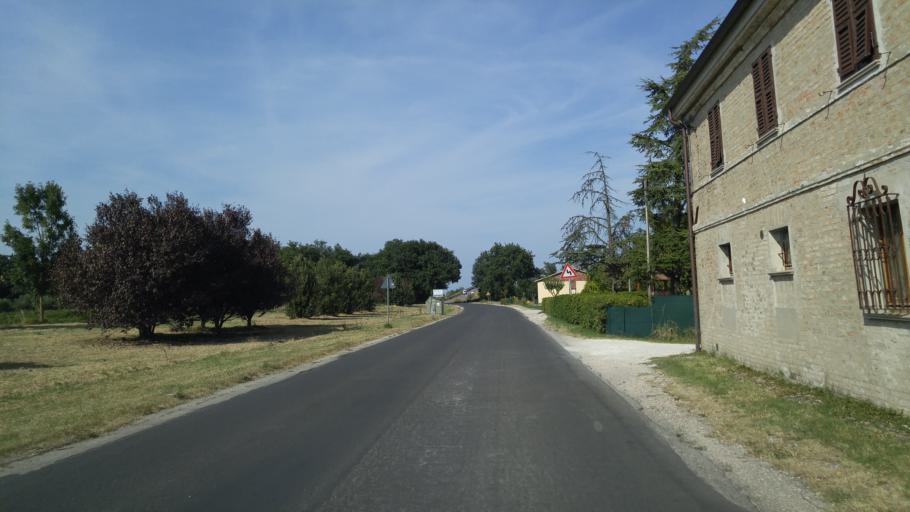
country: IT
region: The Marches
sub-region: Provincia di Pesaro e Urbino
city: Rosciano
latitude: 43.8122
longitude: 13.0060
